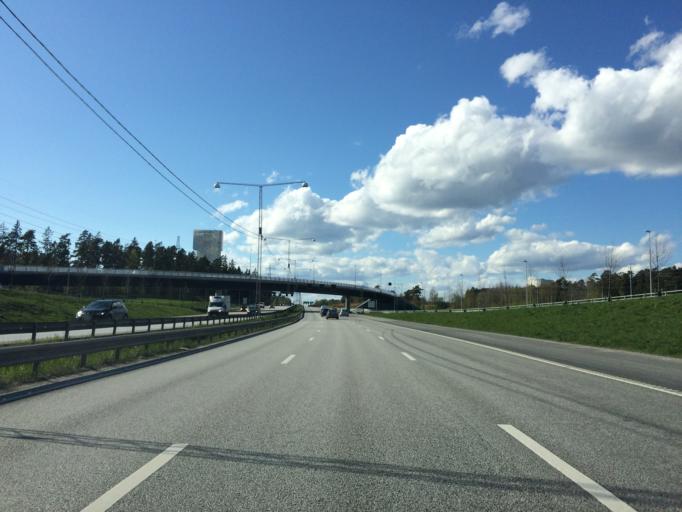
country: SE
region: Stockholm
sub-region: Stockholms Kommun
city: Kista
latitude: 59.4027
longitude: 17.9718
